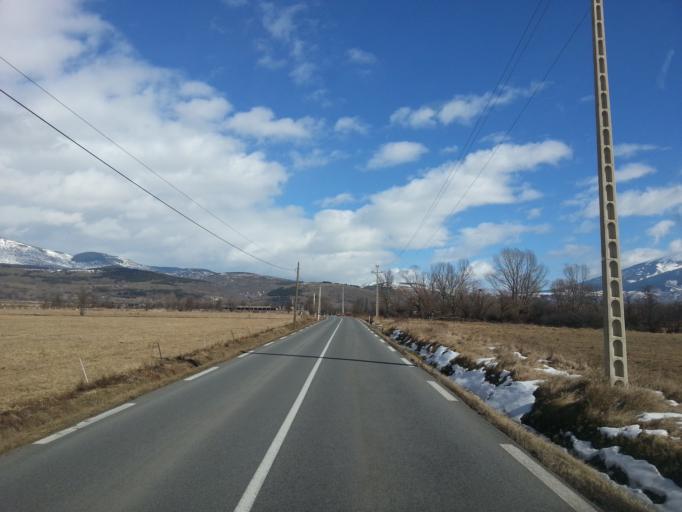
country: FR
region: Languedoc-Roussillon
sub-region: Departement des Pyrenees-Orientales
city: la Guingueta d'Ix
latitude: 42.4517
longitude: 1.9570
